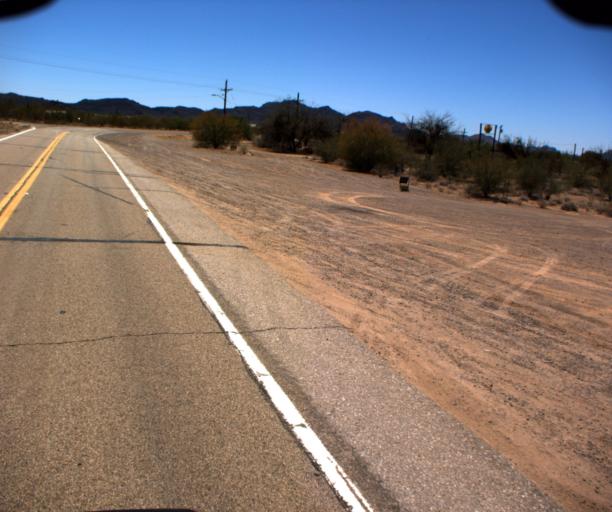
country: US
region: Arizona
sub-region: Pima County
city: Ajo
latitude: 32.2652
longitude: -112.7387
